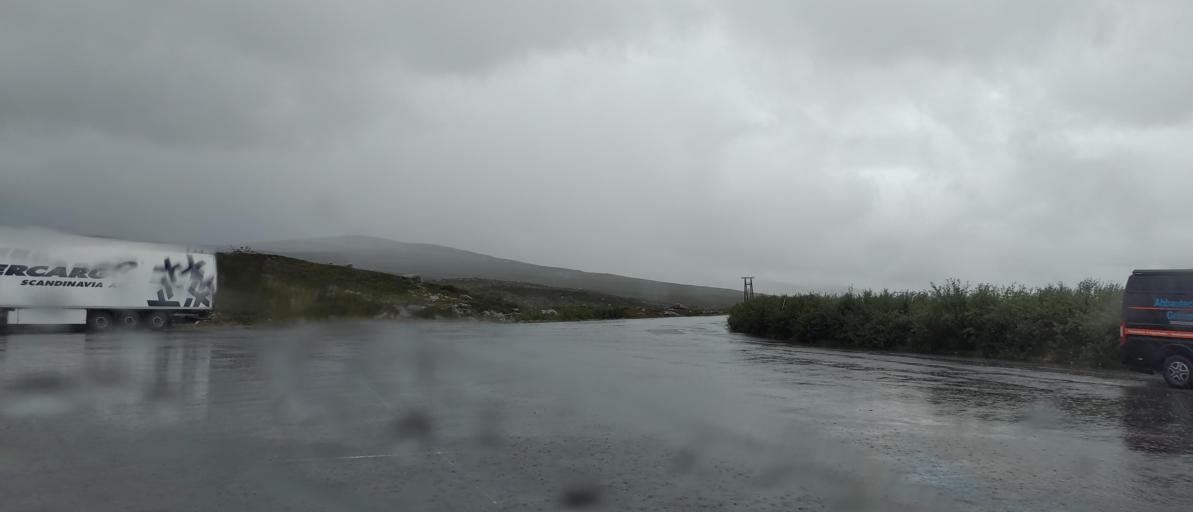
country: NO
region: Nordland
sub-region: Saltdal
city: Rognan
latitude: 66.5516
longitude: 15.3209
